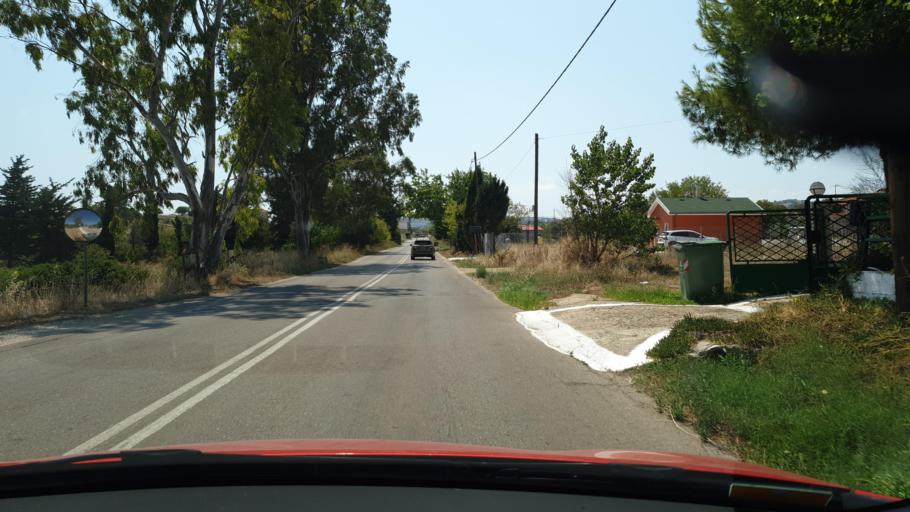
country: GR
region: Central Greece
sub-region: Nomos Evvoias
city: Aliveri
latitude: 38.4721
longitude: 24.1169
